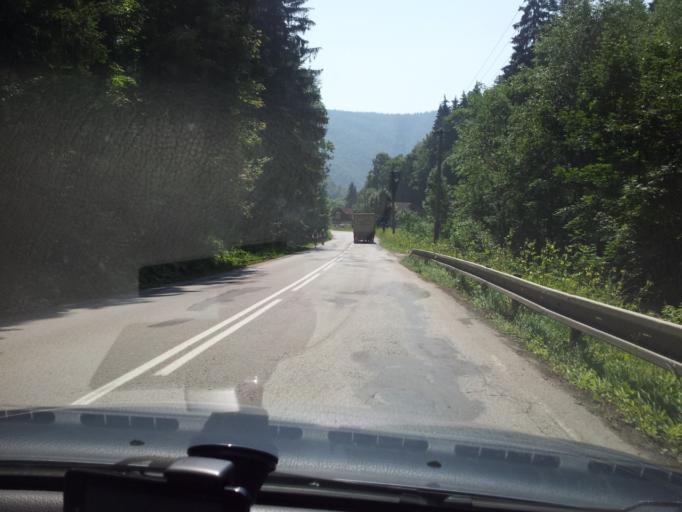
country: SK
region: Zilinsky
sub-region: Okres Dolny Kubin
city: Dolny Kubin
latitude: 49.2687
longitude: 19.3526
